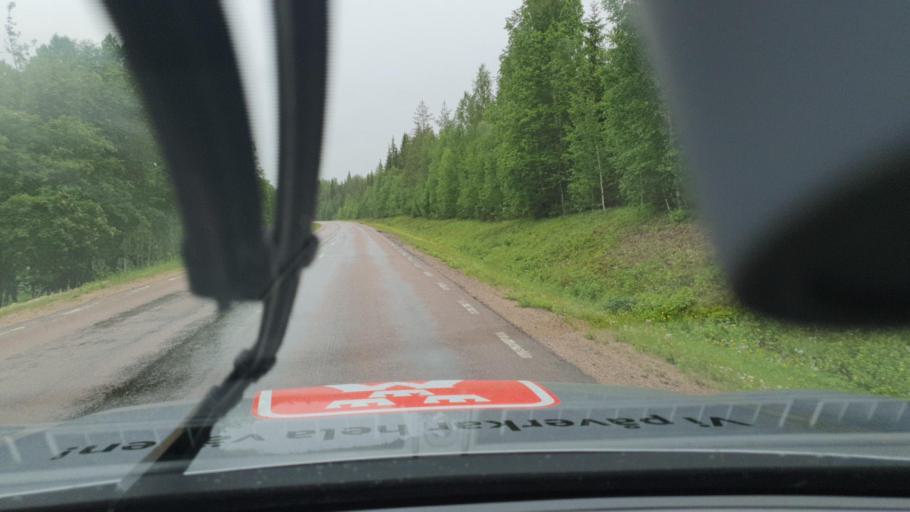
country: SE
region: Norrbotten
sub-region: Overtornea Kommun
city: OEvertornea
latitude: 66.4319
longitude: 23.3371
